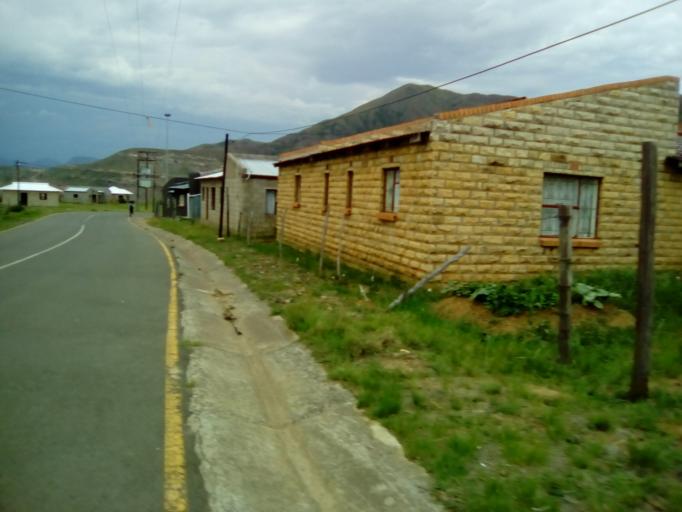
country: LS
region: Qacha's Nek
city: Qacha's Nek
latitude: -30.1064
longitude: 28.6806
